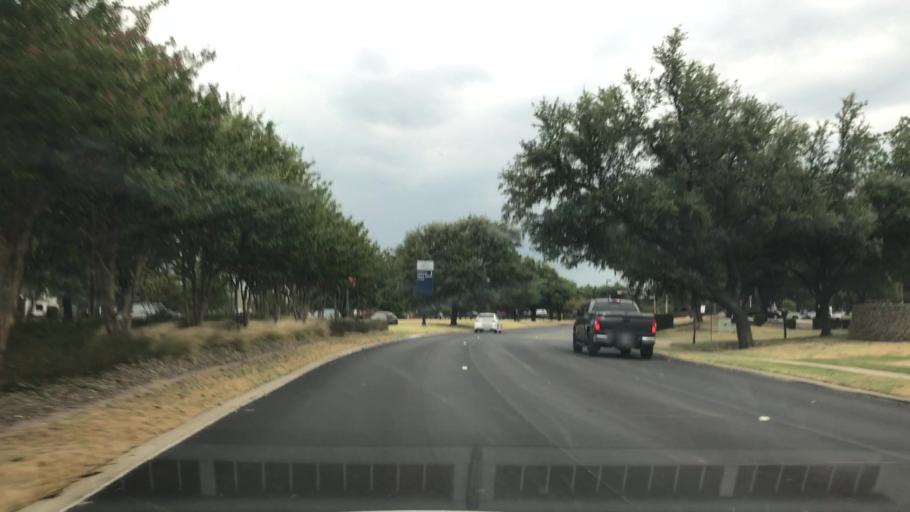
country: US
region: Texas
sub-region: Dallas County
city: Farmers Branch
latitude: 32.9454
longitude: -96.9527
